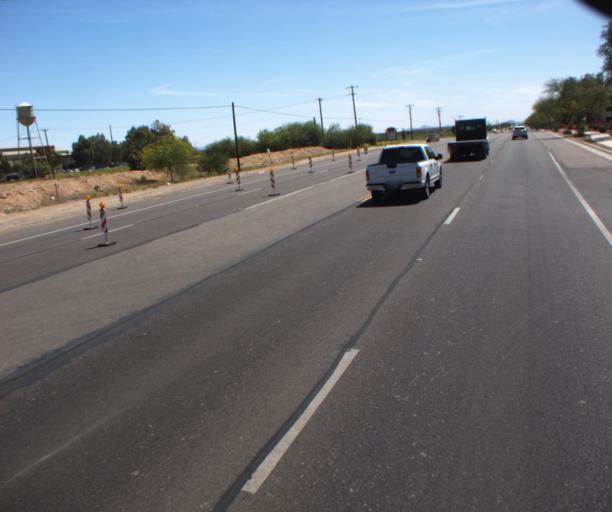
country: US
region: Arizona
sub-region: Maricopa County
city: Sun Lakes
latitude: 33.2315
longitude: -111.8414
